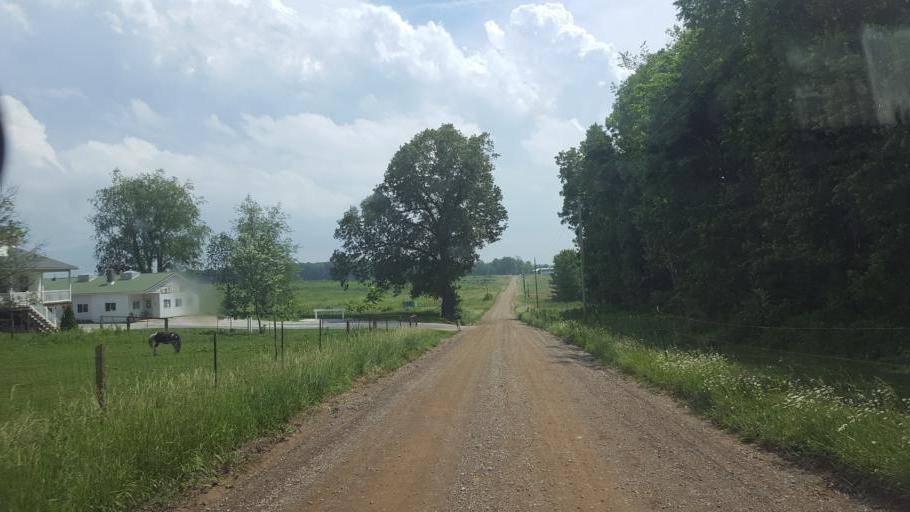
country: US
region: Ohio
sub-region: Knox County
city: Oak Hill
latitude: 40.3280
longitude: -82.2395
